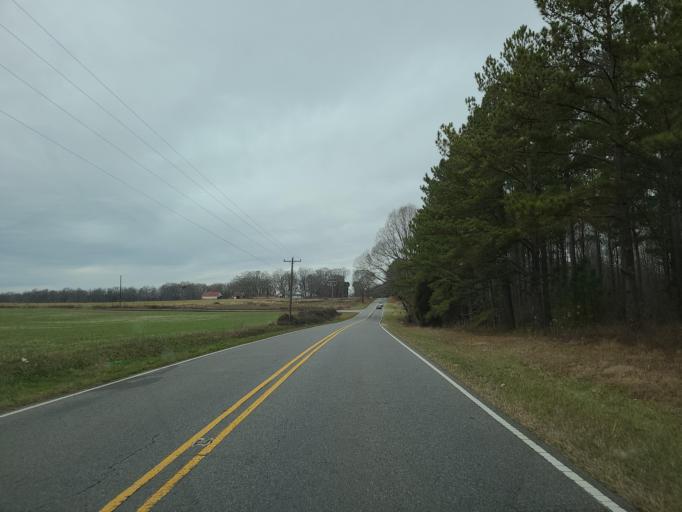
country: US
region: North Carolina
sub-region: Cleveland County
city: Shelby
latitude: 35.3662
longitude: -81.5847
